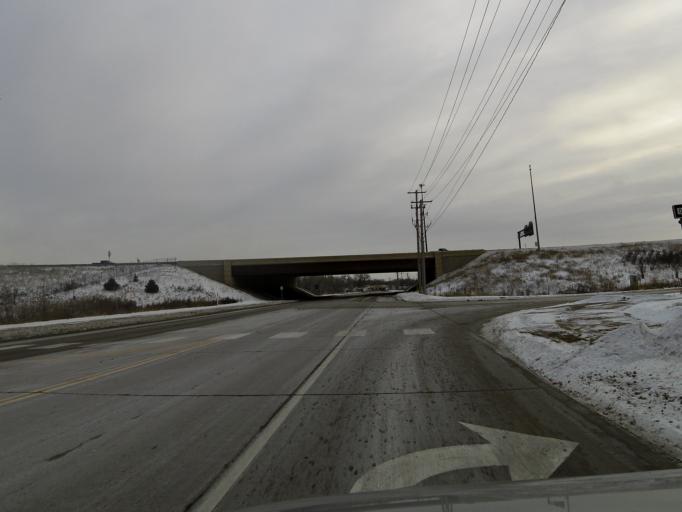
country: US
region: Minnesota
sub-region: Washington County
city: Newport
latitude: 44.8853
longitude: -93.0089
